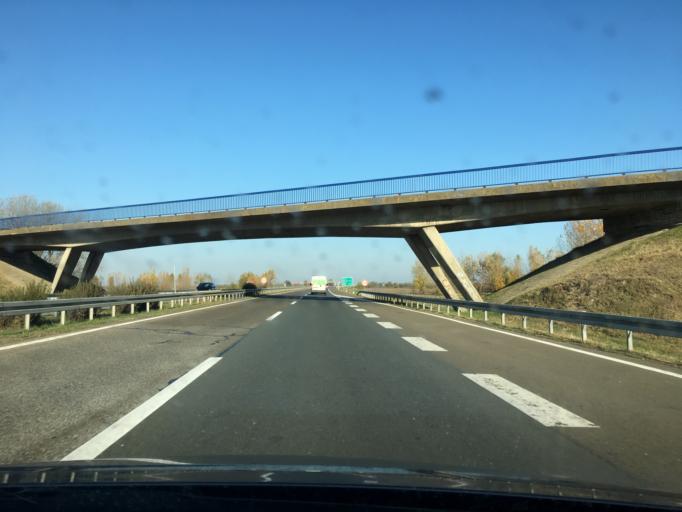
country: RS
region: Autonomna Pokrajina Vojvodina
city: Nova Pazova
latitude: 44.9863
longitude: 20.2156
